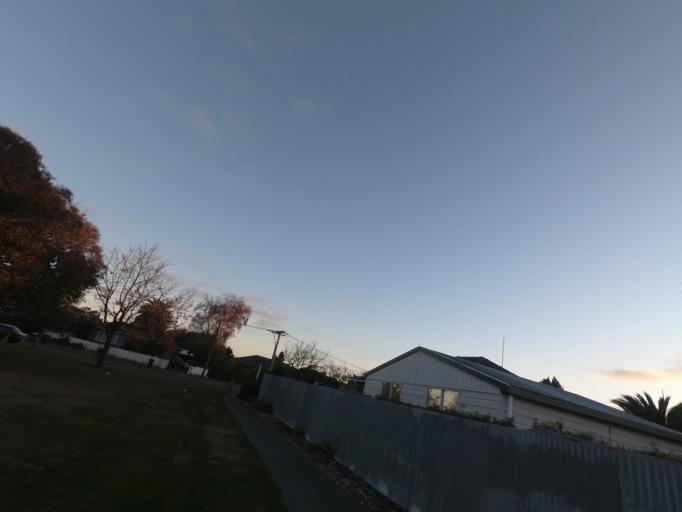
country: NZ
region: Canterbury
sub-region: Selwyn District
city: Prebbleton
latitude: -43.5750
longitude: 172.5621
